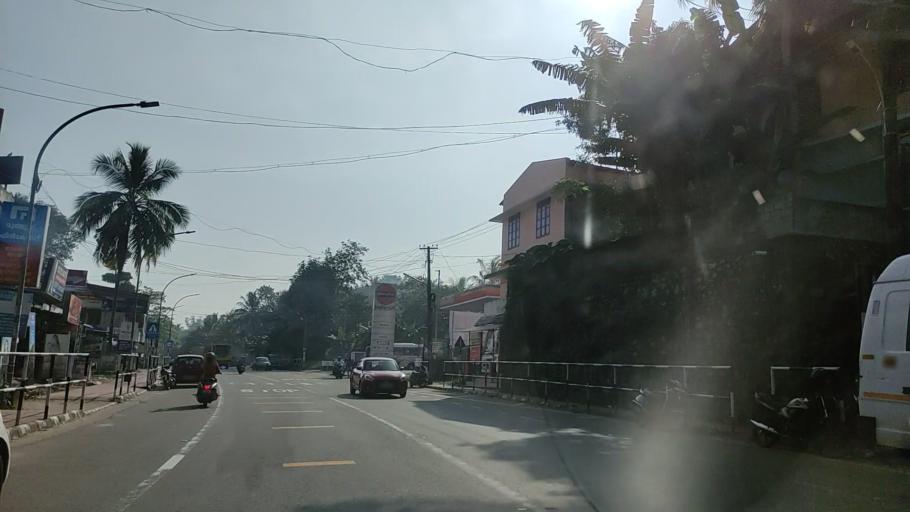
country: IN
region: Kerala
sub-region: Kollam
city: Punalur
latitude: 8.9728
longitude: 76.8236
